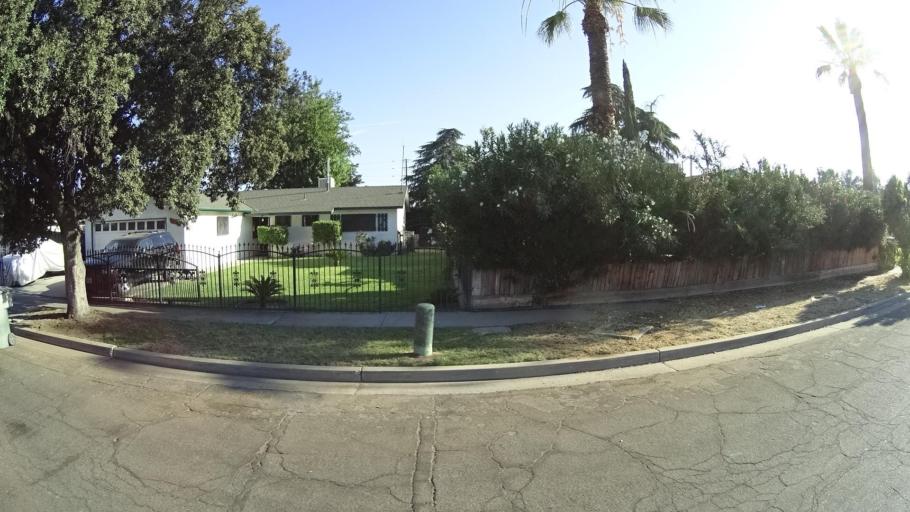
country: US
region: California
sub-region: Fresno County
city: Sunnyside
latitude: 36.7424
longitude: -119.7301
